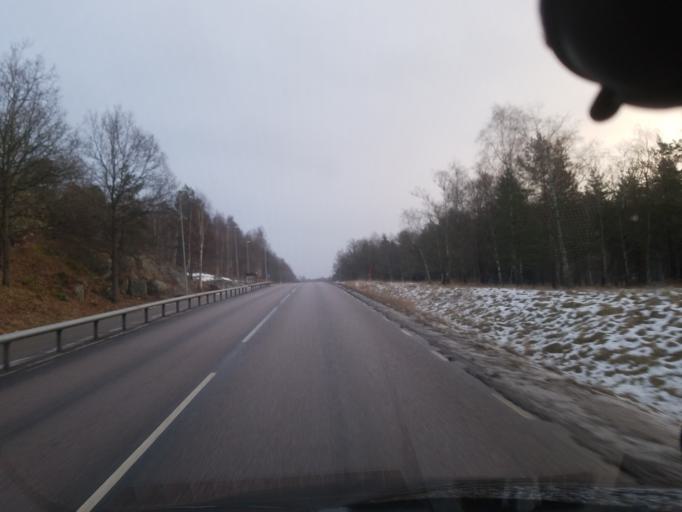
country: SE
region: Vaestra Goetaland
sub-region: Uddevalla Kommun
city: Uddevalla
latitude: 58.3552
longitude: 11.8758
